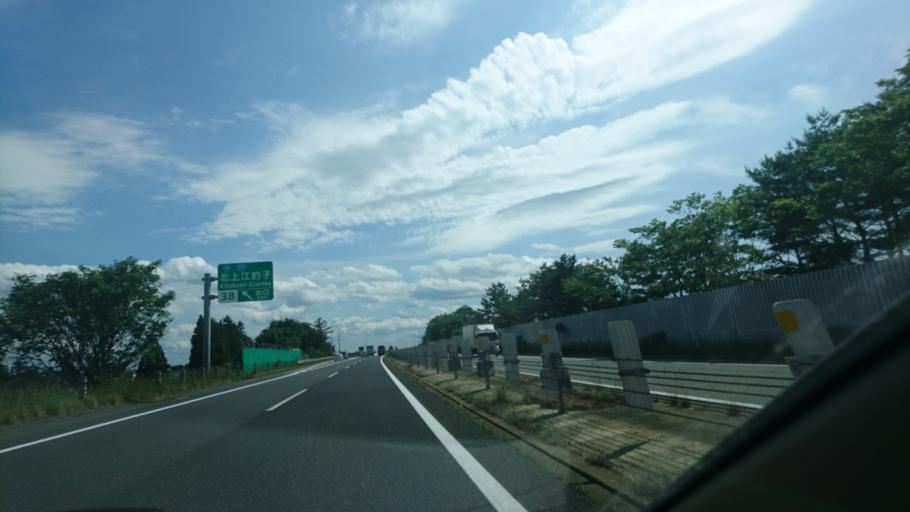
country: JP
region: Iwate
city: Kitakami
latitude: 39.3022
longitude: 141.0890
